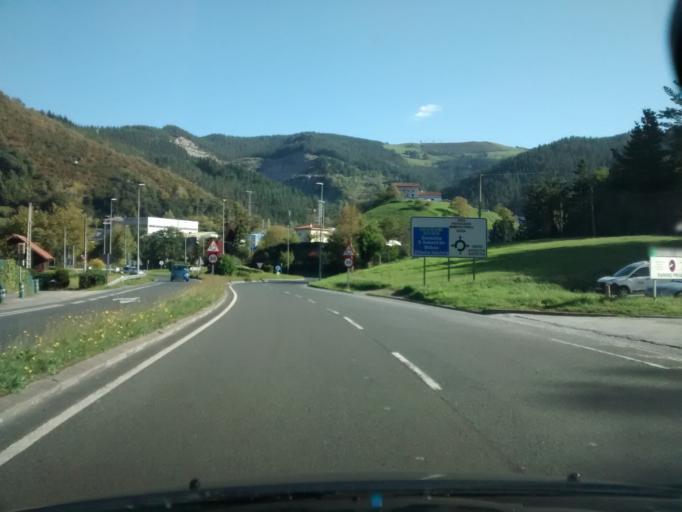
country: ES
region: Basque Country
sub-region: Provincia de Guipuzcoa
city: Elgoibar
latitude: 43.2280
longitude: -2.4024
